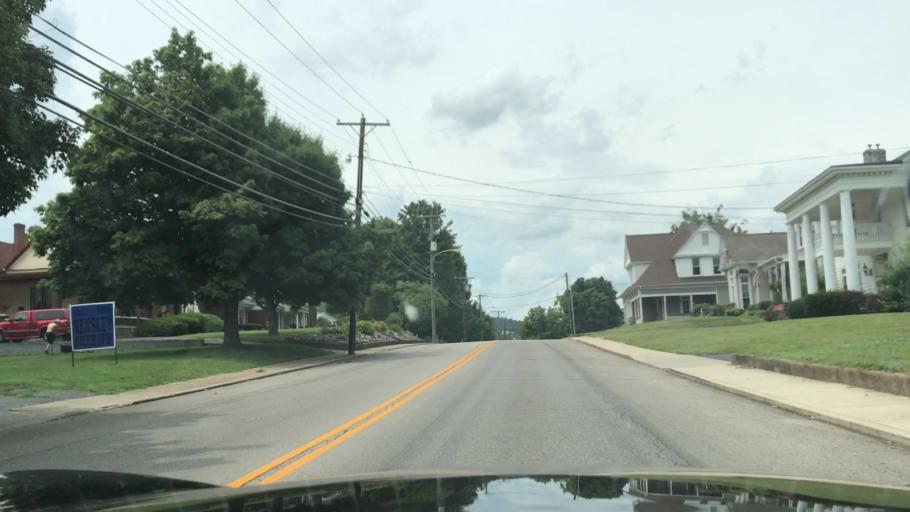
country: US
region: Kentucky
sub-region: Hart County
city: Horse Cave
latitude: 37.1790
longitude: -85.9011
